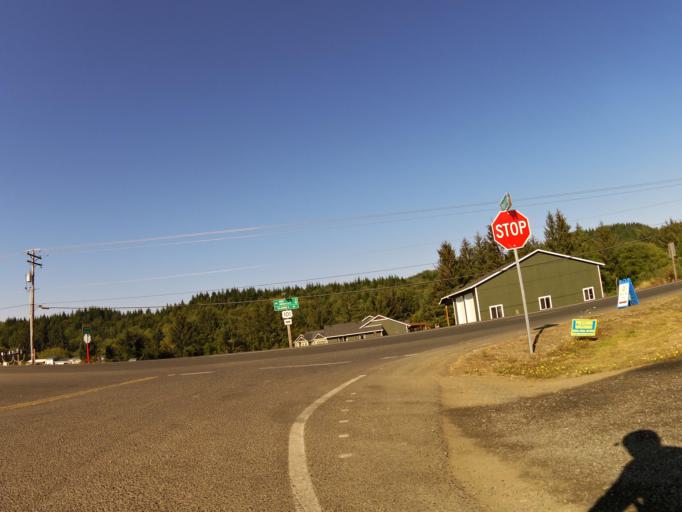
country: US
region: Oregon
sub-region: Tillamook County
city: Tillamook
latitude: 45.3846
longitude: -123.8051
